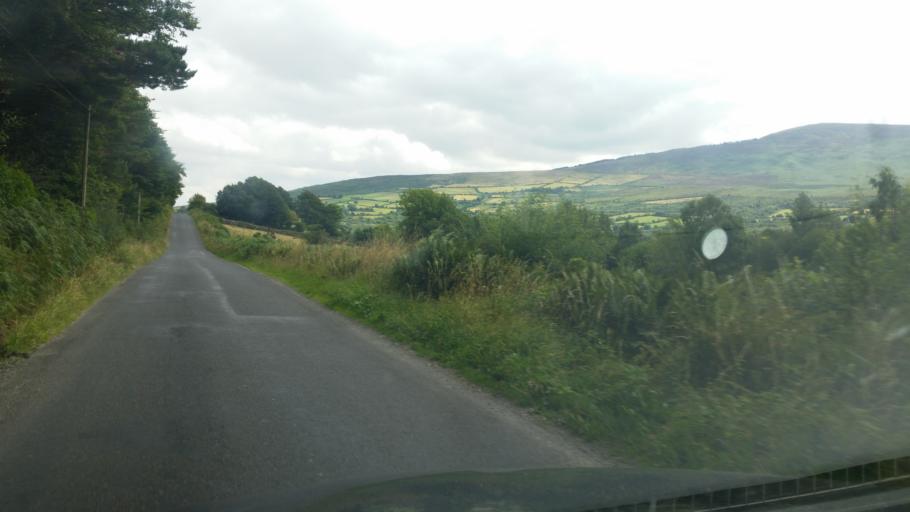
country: IE
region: Leinster
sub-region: Loch Garman
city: Bunclody
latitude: 52.6462
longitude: -6.7239
